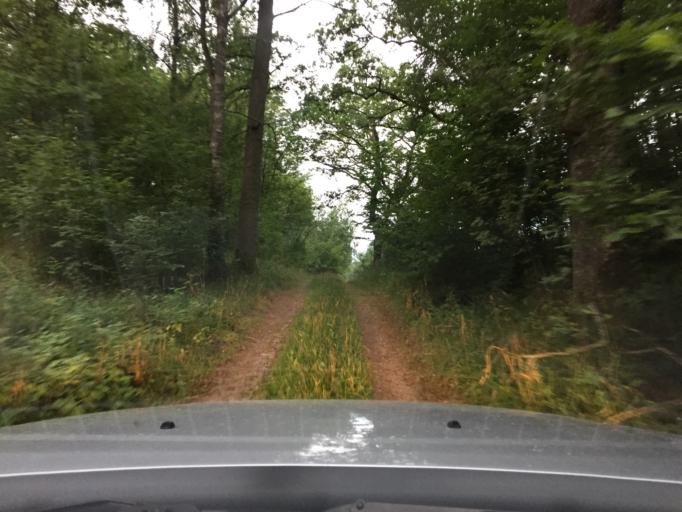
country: SE
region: Skane
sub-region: Hassleholms Kommun
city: Sosdala
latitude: 56.0421
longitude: 13.6970
